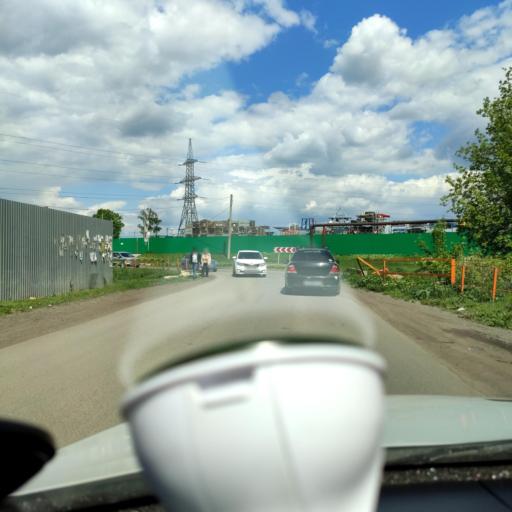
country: RU
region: Samara
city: Petra-Dubrava
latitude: 53.2647
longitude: 50.3173
